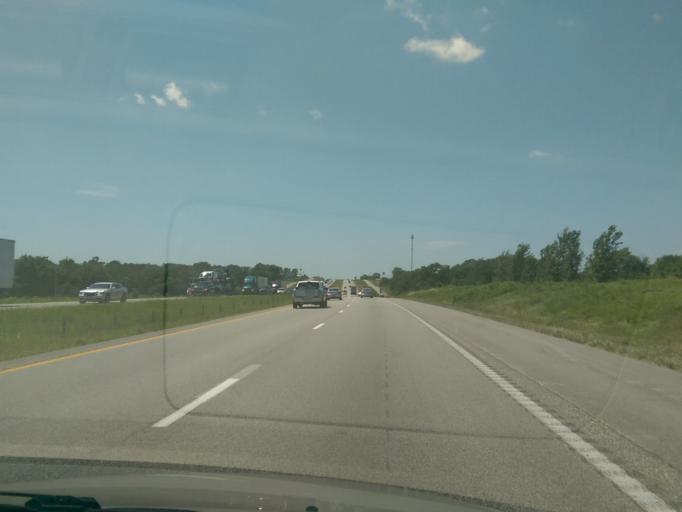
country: US
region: Missouri
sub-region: Saline County
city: Sweet Springs
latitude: 38.9710
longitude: -93.2560
